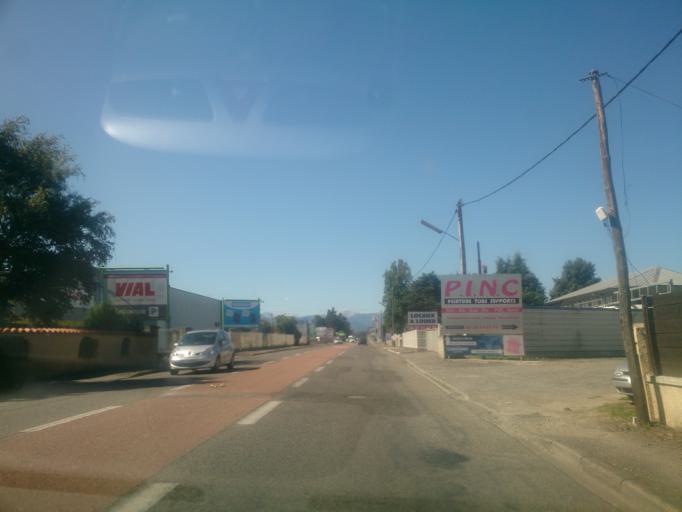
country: FR
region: Midi-Pyrenees
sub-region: Departement des Hautes-Pyrenees
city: Odos
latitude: 43.2151
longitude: 0.0533
